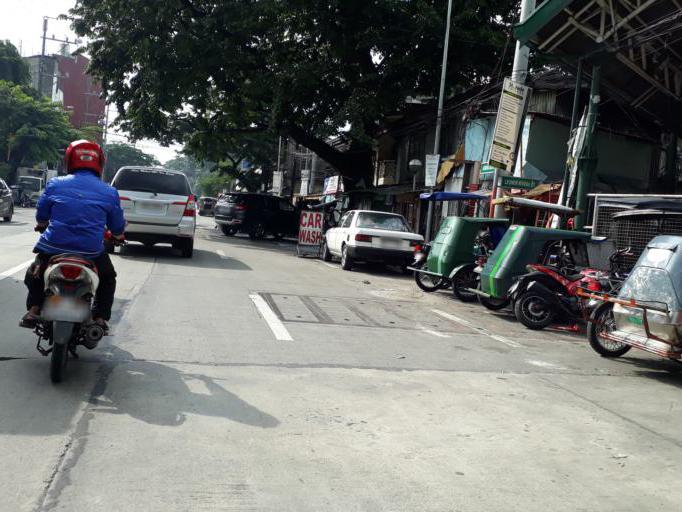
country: PH
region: Metro Manila
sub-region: City of Manila
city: Manila
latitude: 14.6259
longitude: 120.9868
